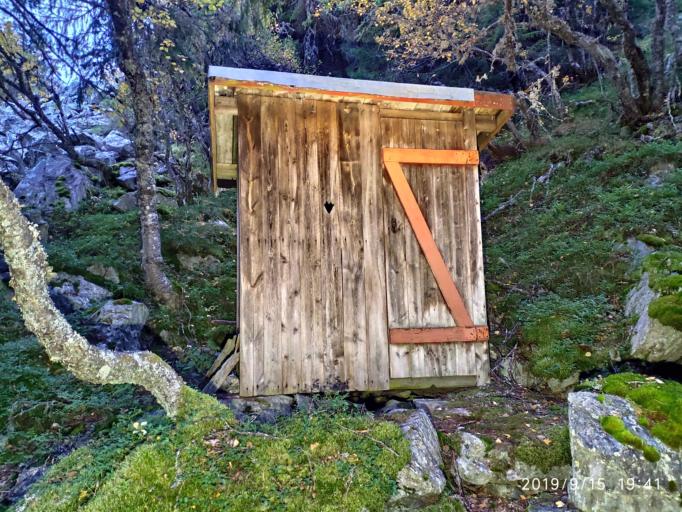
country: NO
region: Oppland
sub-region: Oyer
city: Tretten
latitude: 61.4238
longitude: 10.2629
